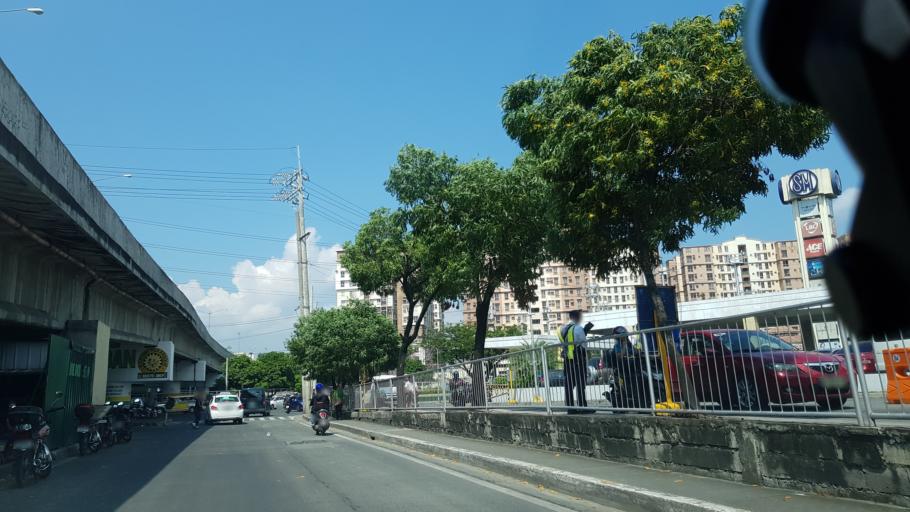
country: PH
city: Sambayanihan People's Village
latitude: 14.4842
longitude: 120.9930
